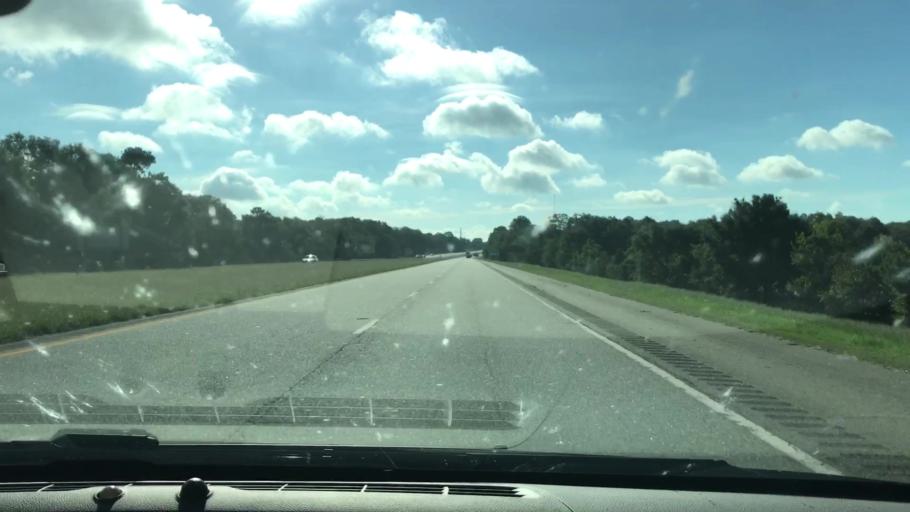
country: US
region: Georgia
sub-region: Dougherty County
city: Albany
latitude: 31.6131
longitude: -84.1674
